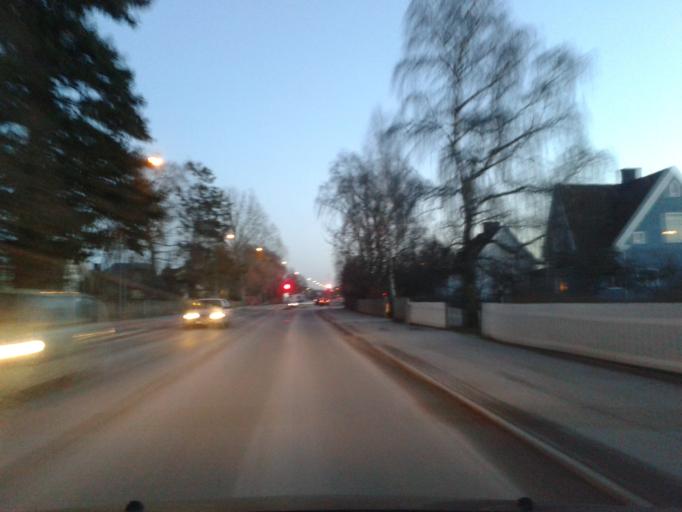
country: SE
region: Gotland
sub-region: Gotland
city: Visby
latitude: 57.6337
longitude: 18.3094
